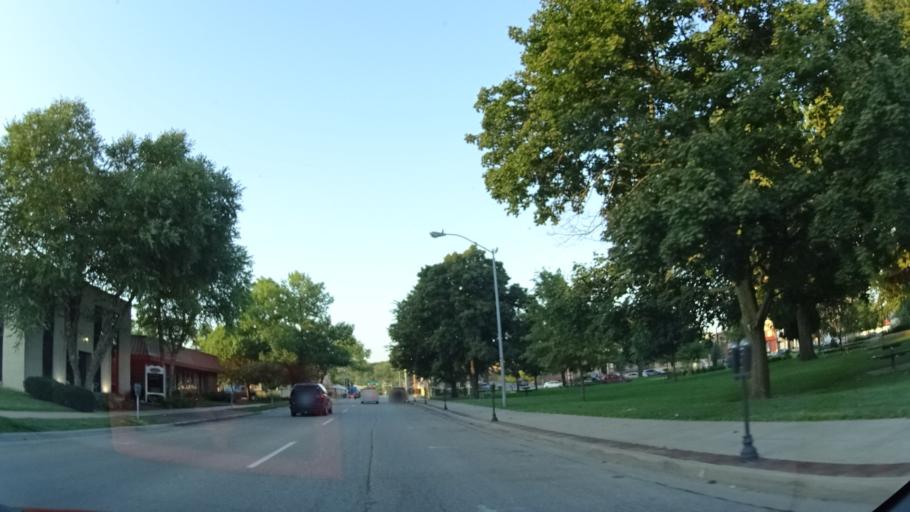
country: US
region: Iowa
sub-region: Pottawattamie County
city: Council Bluffs
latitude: 41.2591
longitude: -95.8526
